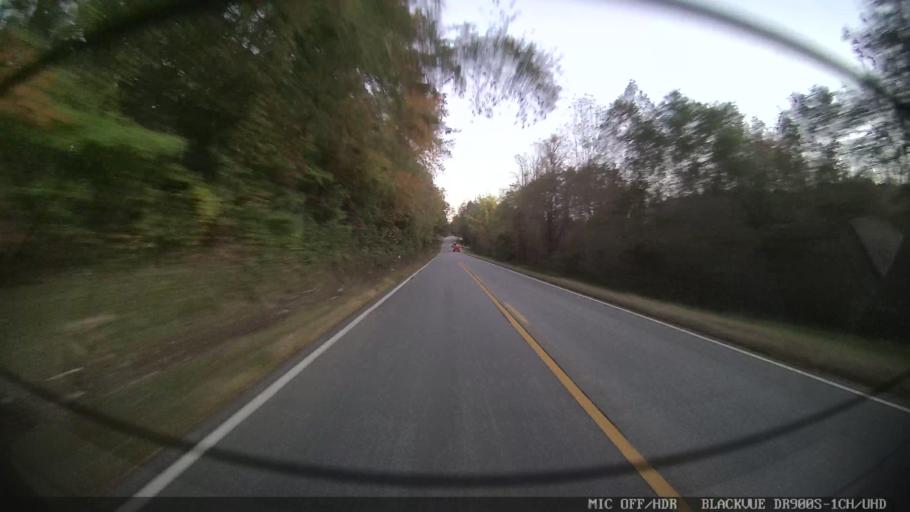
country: US
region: North Carolina
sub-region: Clay County
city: Hayesville
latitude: 34.9633
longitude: -83.8727
